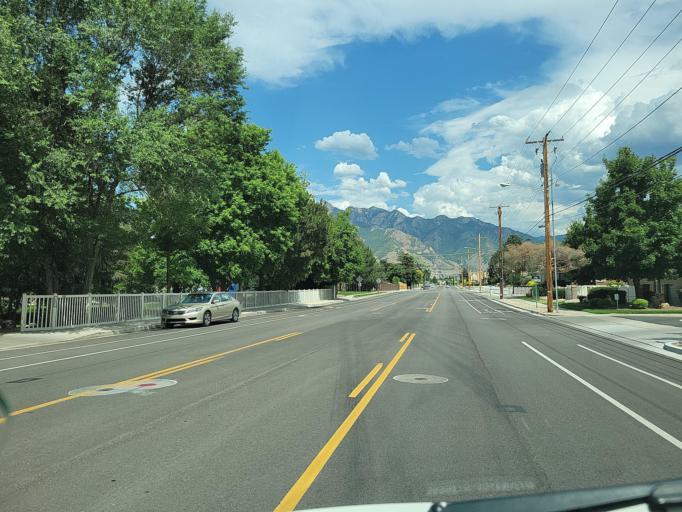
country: US
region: Utah
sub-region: Salt Lake County
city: Murray
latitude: 40.6406
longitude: -111.8605
